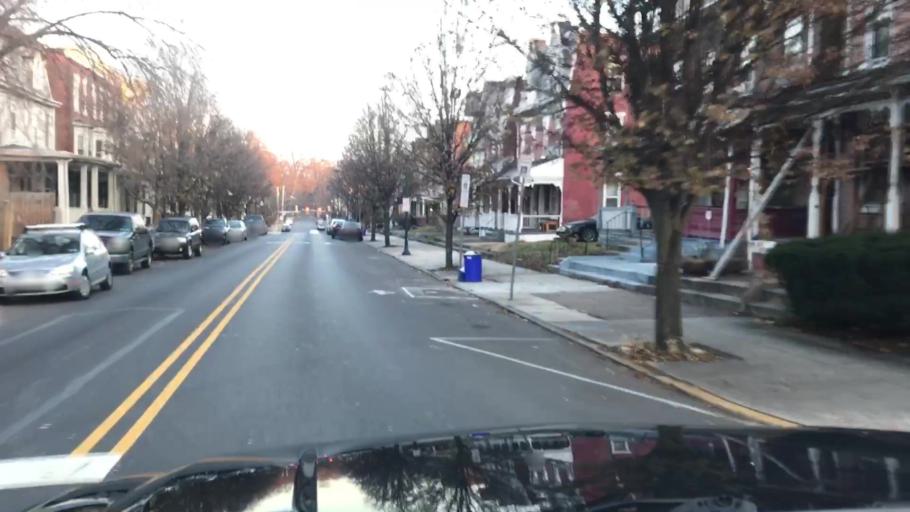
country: US
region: Pennsylvania
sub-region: Dauphin County
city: Harrisburg
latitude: 40.2678
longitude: -76.8710
